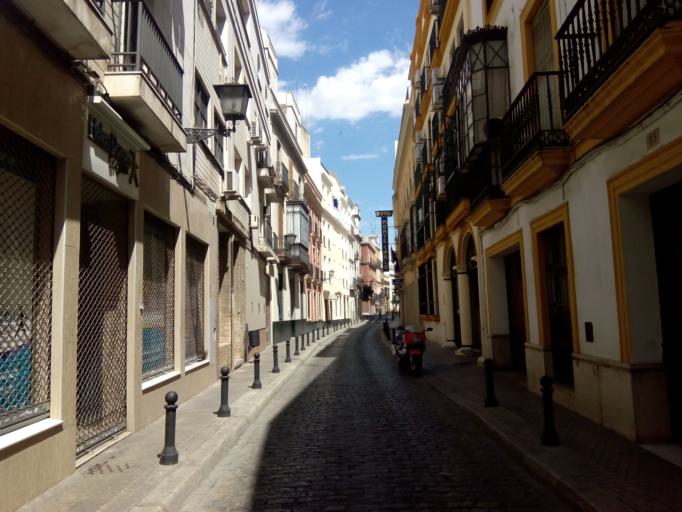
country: ES
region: Andalusia
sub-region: Provincia de Sevilla
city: Sevilla
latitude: 37.3897
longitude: -5.9998
